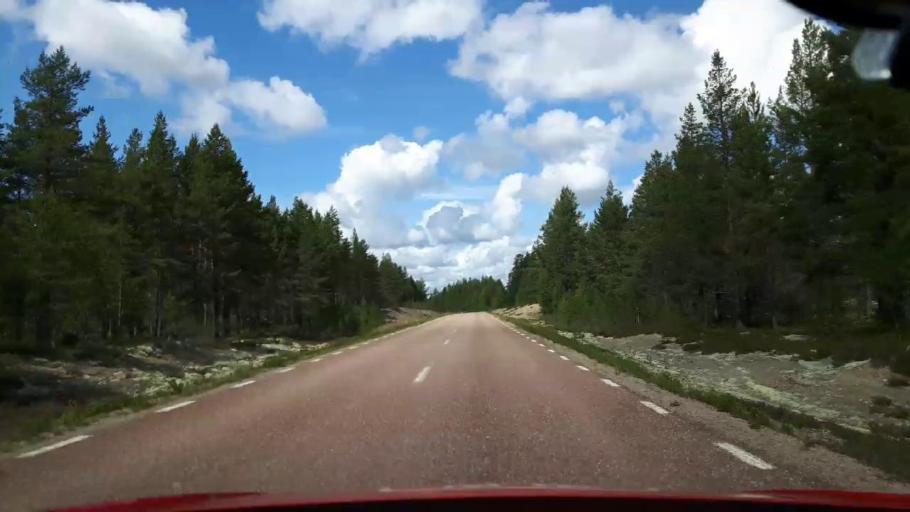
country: SE
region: Dalarna
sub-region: Alvdalens Kommun
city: AElvdalen
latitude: 61.8038
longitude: 13.6569
